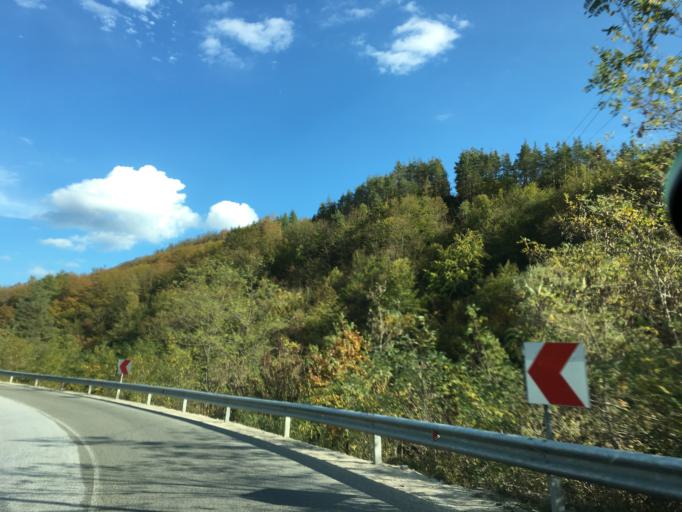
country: BG
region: Smolyan
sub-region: Obshtina Madan
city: Madan
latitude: 41.5353
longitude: 24.9201
